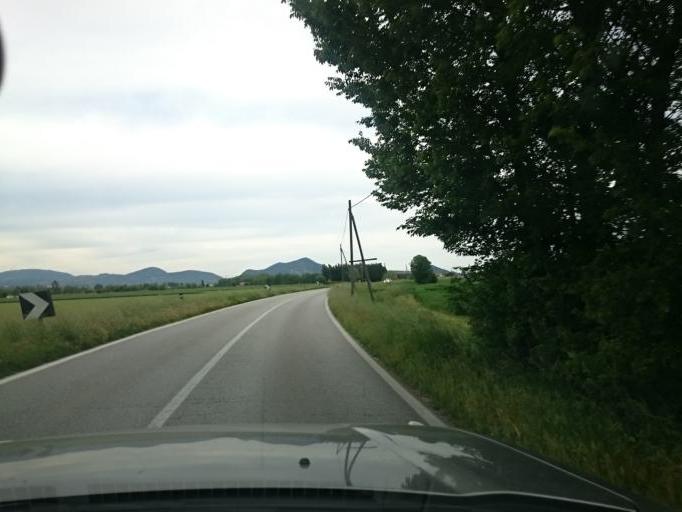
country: IT
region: Veneto
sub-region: Provincia di Padova
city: Sant'Elena
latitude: 45.1975
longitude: 11.7167
